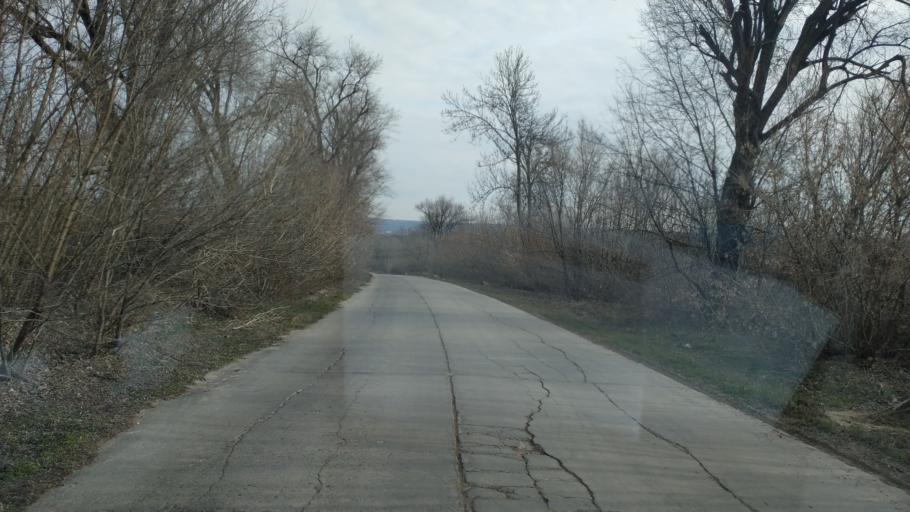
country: MD
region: Chisinau
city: Vadul lui Voda
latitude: 46.9954
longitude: 29.1082
